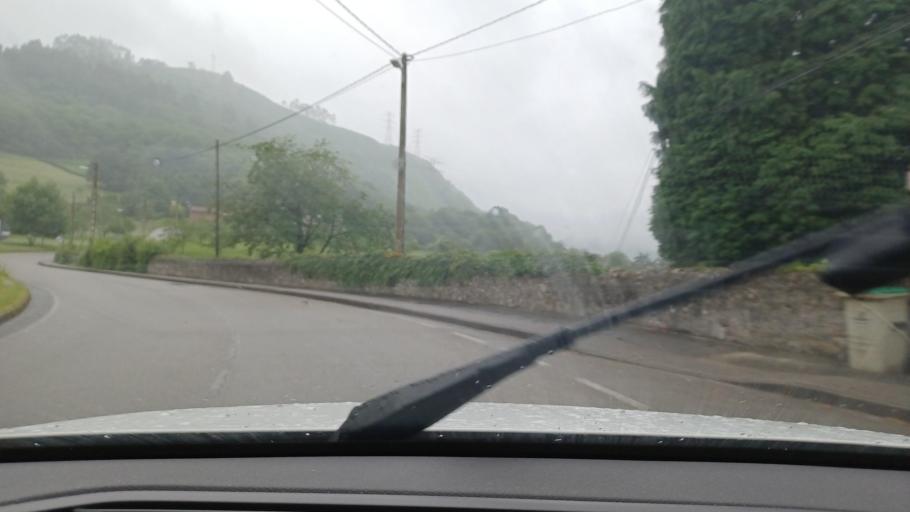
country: ES
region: Asturias
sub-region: Province of Asturias
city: Castandiello
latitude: 43.3098
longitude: -5.8877
